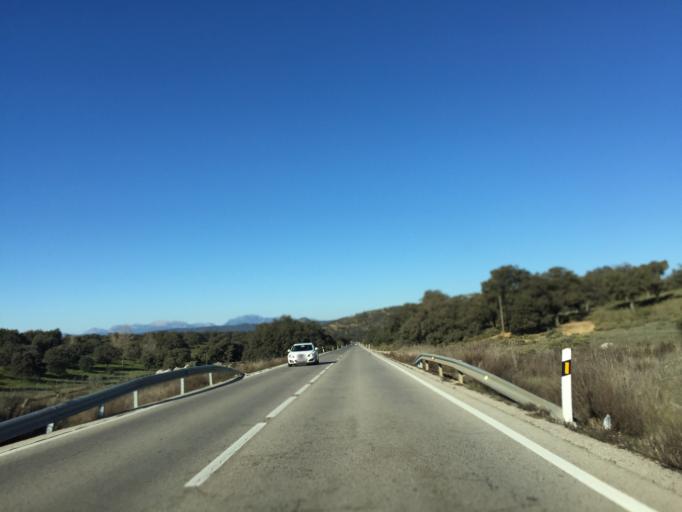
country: ES
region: Andalusia
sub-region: Provincia de Malaga
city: Cuevas del Becerro
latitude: 36.8319
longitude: -5.0747
